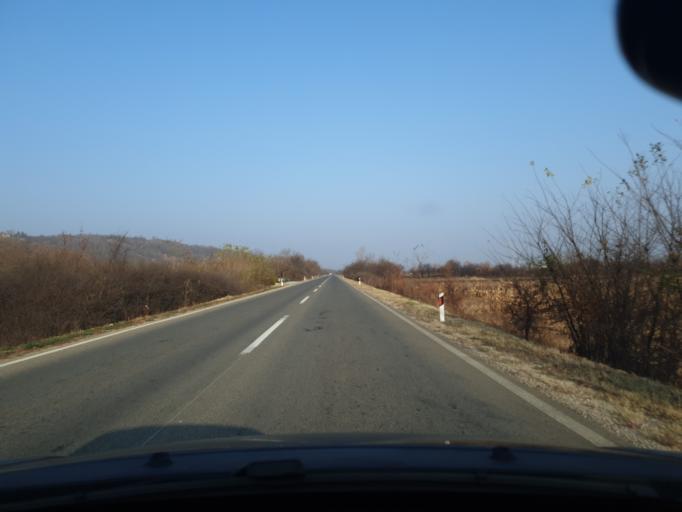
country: RS
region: Central Serbia
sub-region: Jablanicki Okrug
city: Leskovac
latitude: 42.9589
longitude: 21.9847
